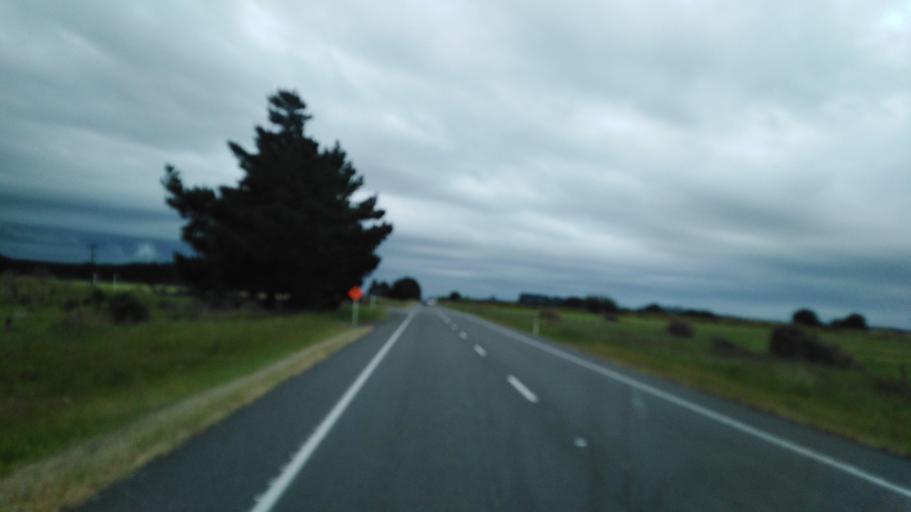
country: NZ
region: Manawatu-Wanganui
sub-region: Horowhenua District
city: Foxton
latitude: -40.4231
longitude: 175.3042
